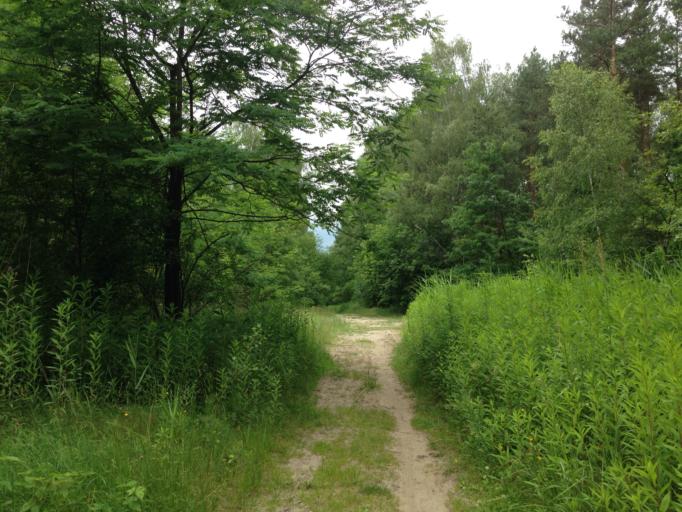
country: PL
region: Masovian Voivodeship
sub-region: Powiat warszawski zachodni
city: Babice
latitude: 52.2620
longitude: 20.8746
